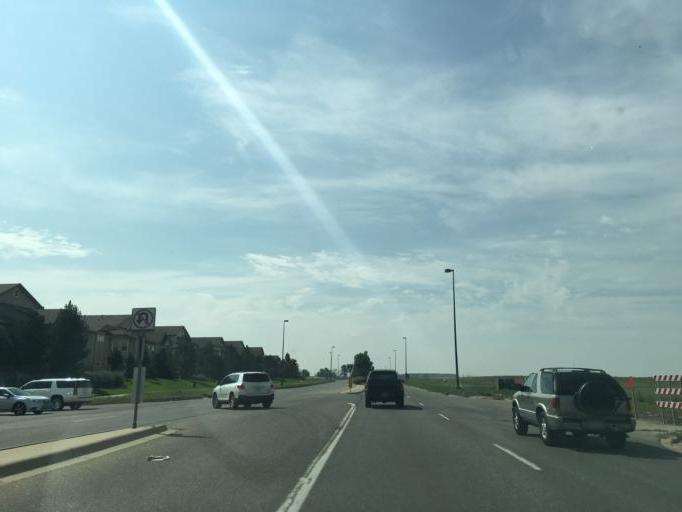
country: US
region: Colorado
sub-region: Adams County
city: Aurora
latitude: 39.8044
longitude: -104.7722
